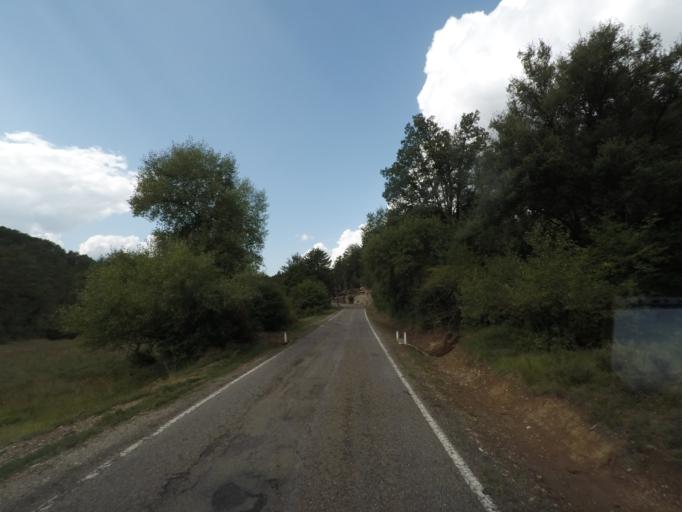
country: ES
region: Aragon
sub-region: Provincia de Huesca
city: Fiscal
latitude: 42.4054
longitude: -0.1803
